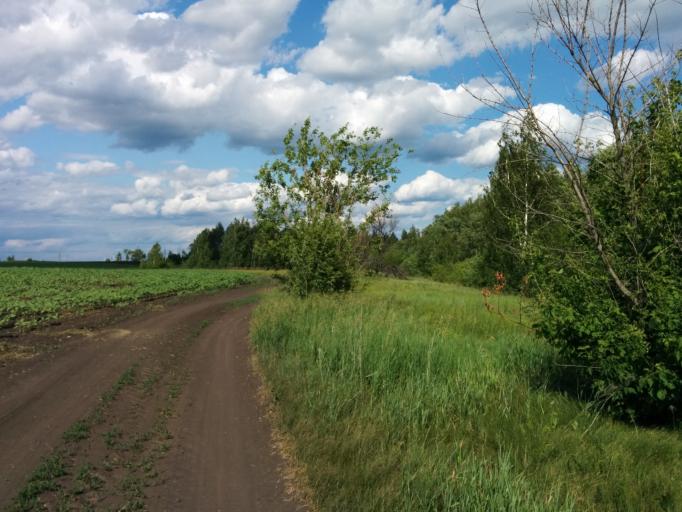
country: RU
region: Tambov
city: Donskoye
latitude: 52.8067
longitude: 41.3938
